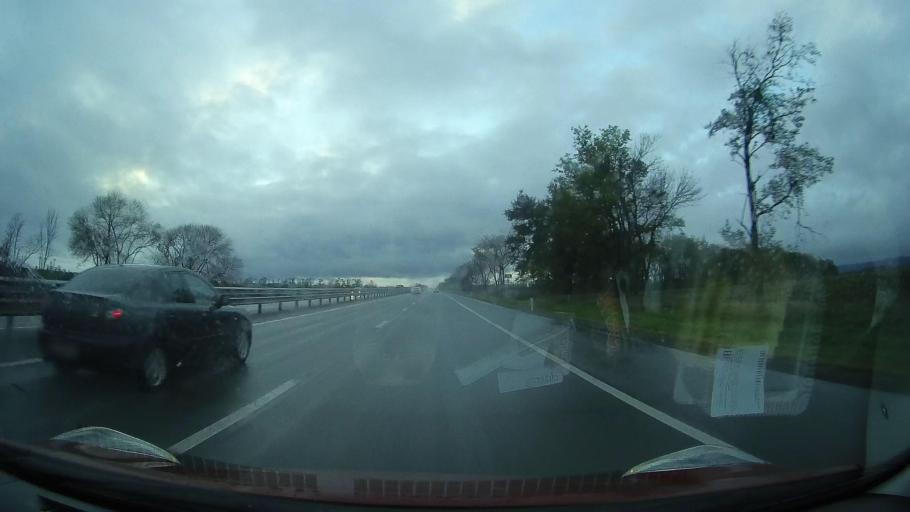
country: RU
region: Stavropol'skiy
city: Zavetnoye
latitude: 44.7878
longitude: 41.5086
